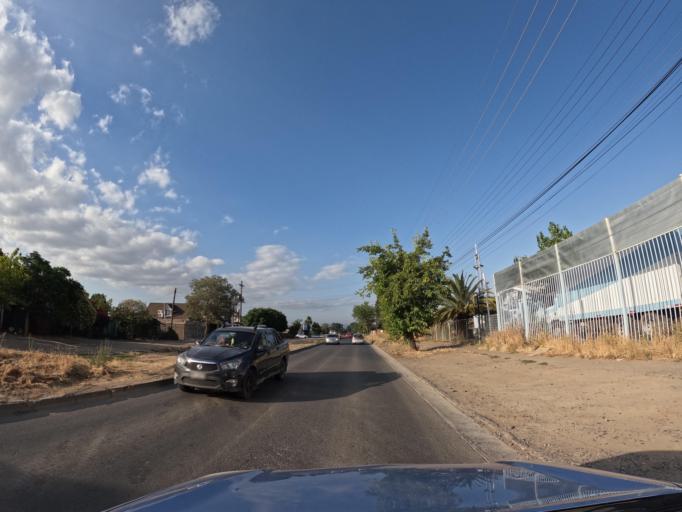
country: CL
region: Maule
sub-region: Provincia de Talca
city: Talca
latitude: -35.4462
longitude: -71.6486
